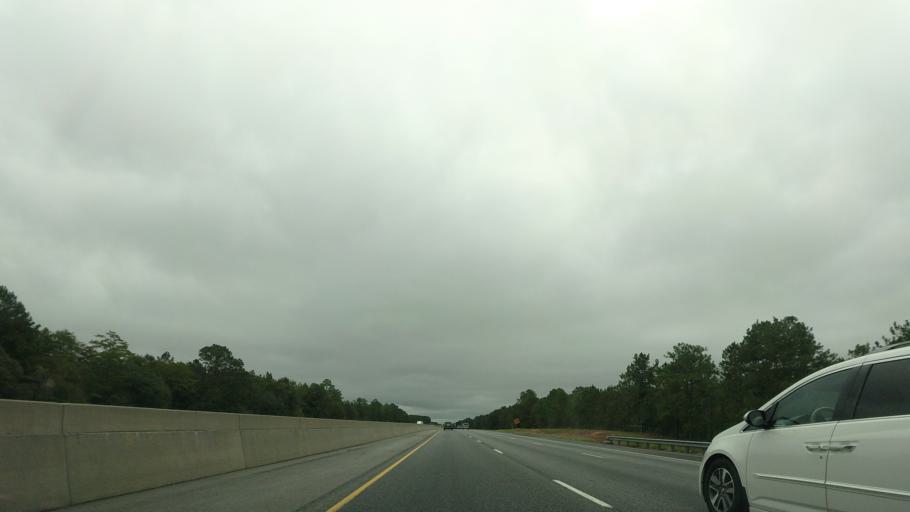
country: US
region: Georgia
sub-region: Turner County
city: Ashburn
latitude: 31.7688
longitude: -83.6770
